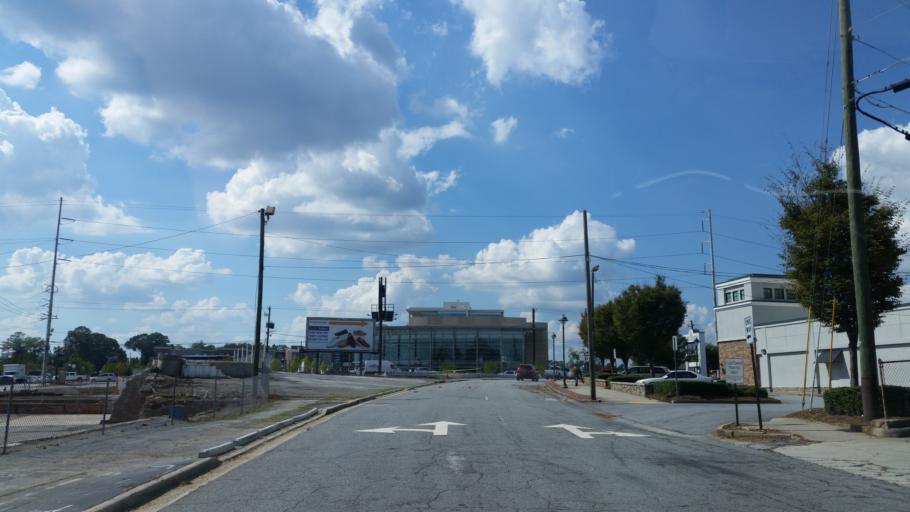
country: US
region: Georgia
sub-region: Fulton County
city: Sandy Springs
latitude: 33.9246
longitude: -84.3777
